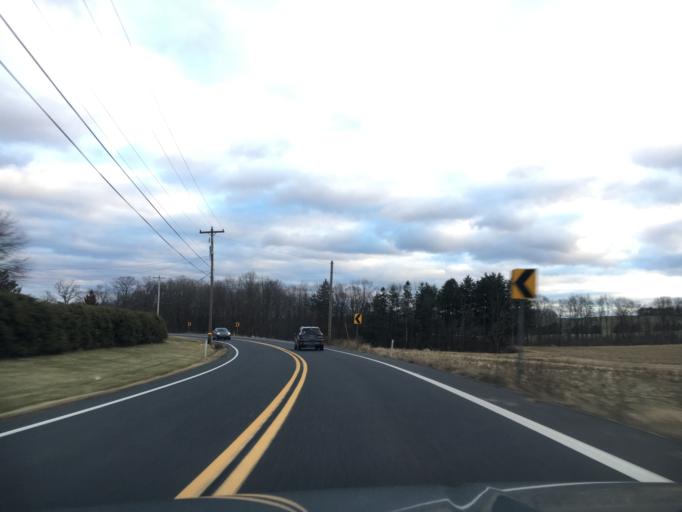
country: US
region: Pennsylvania
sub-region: Lehigh County
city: Schnecksville
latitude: 40.6830
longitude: -75.6631
